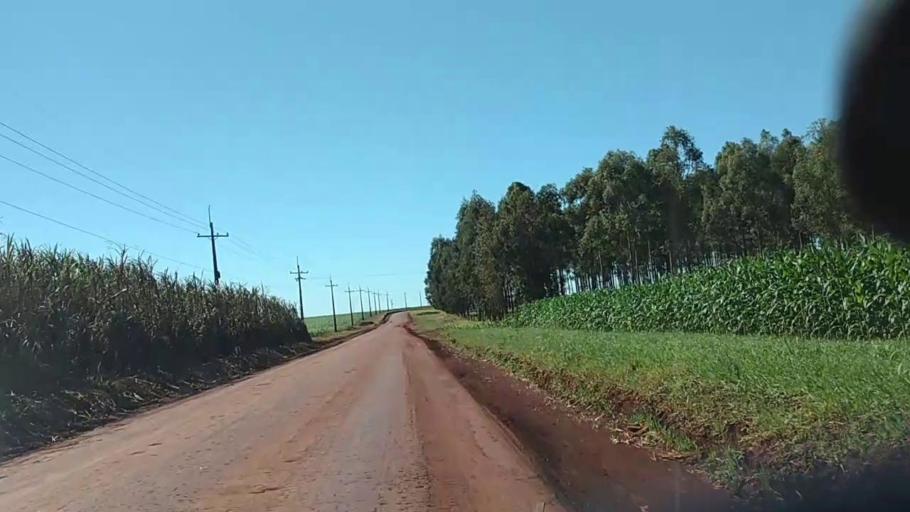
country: PY
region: Alto Parana
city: Naranjal
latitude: -25.9403
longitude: -55.3034
